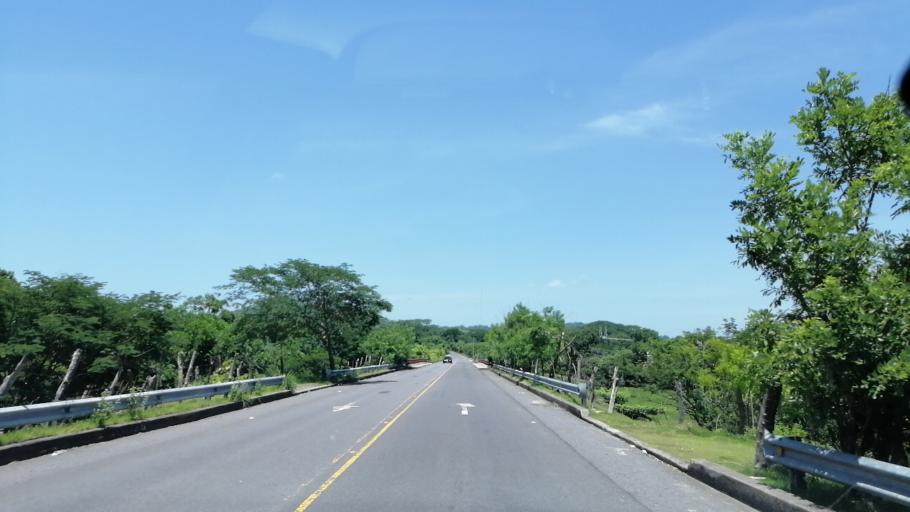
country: SV
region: Chalatenango
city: Chalatenango
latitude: 14.0375
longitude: -88.9659
